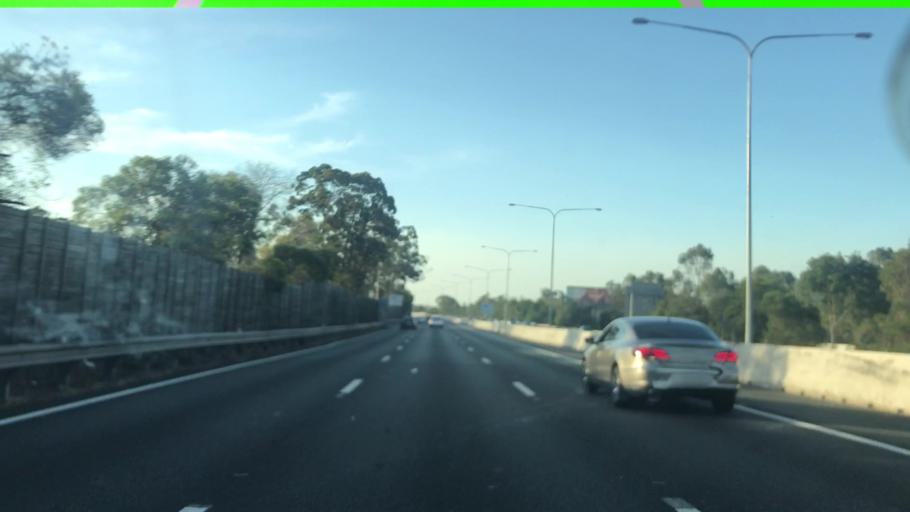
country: AU
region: Queensland
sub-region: Brisbane
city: Greenslopes
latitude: -27.5310
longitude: 153.0574
